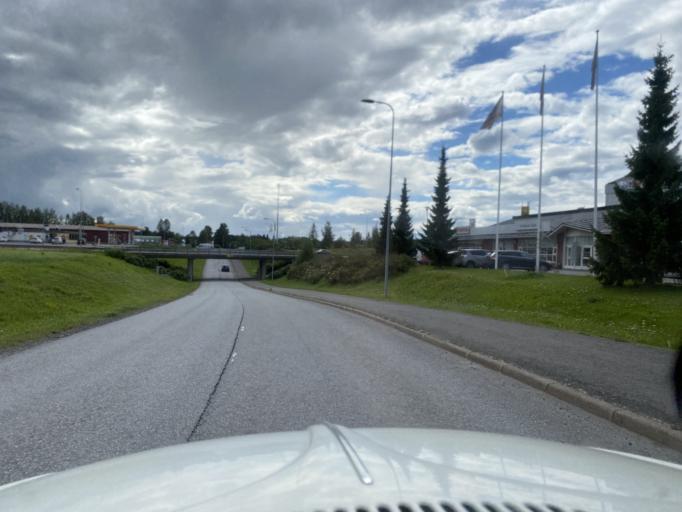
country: FI
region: Satakunta
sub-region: Pori
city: Huittinen
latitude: 61.1694
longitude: 22.6834
